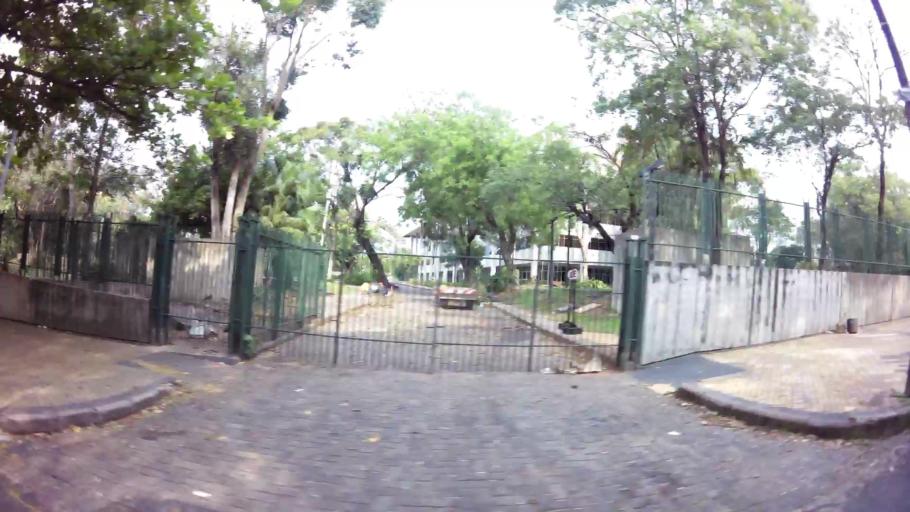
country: PY
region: Asuncion
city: Asuncion
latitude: -25.2874
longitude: -57.6126
